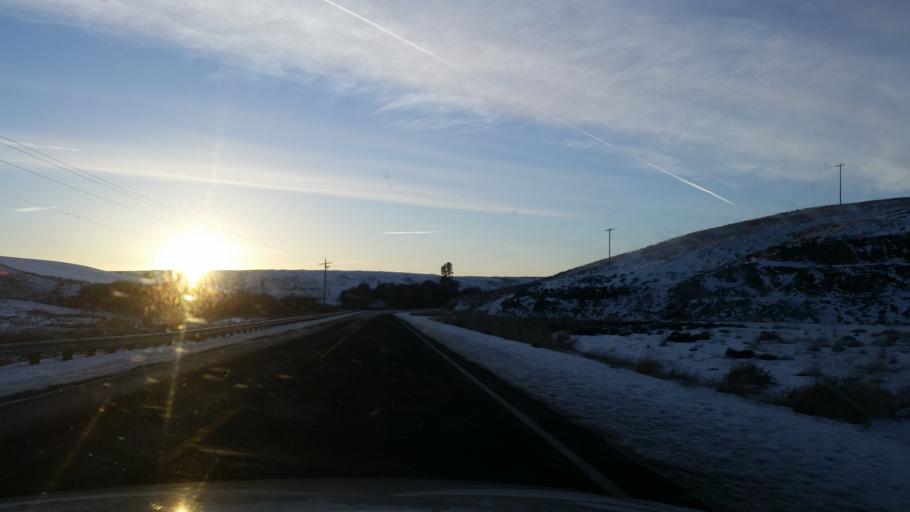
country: US
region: Washington
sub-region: Spokane County
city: Cheney
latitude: 47.1124
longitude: -117.7026
